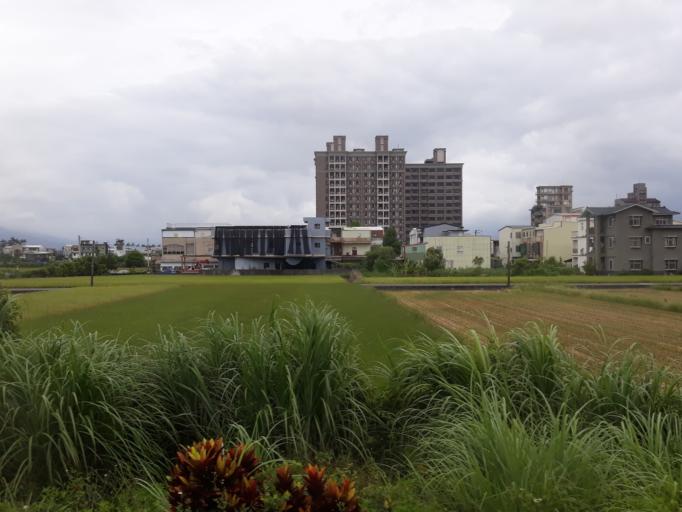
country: TW
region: Taiwan
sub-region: Yilan
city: Yilan
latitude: 24.6902
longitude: 121.7750
